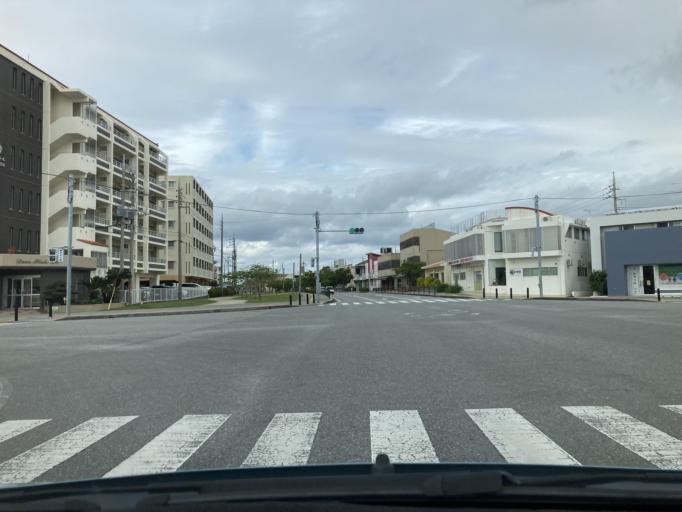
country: JP
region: Okinawa
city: Itoman
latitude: 26.1551
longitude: 127.6621
